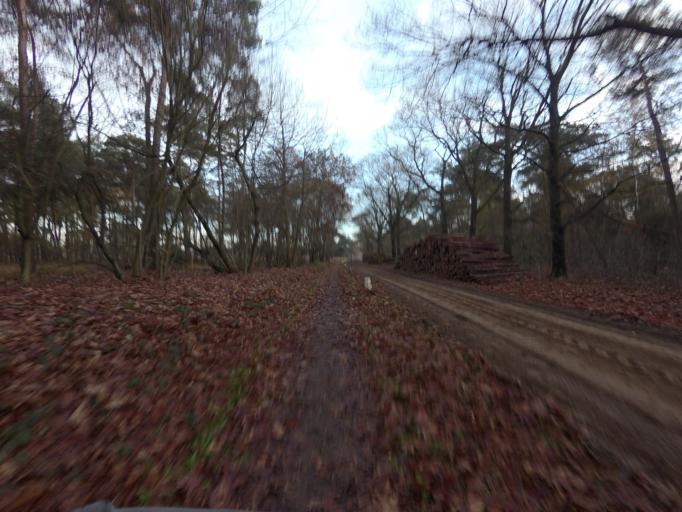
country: NL
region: North Brabant
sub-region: Gemeente Breda
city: Breda
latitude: 51.5078
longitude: 4.8142
